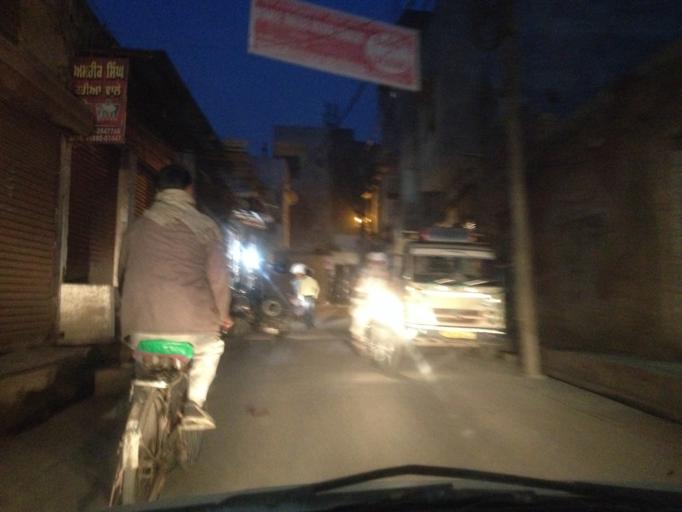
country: IN
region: Punjab
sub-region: Amritsar
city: Amritsar
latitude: 31.6189
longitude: 74.8836
